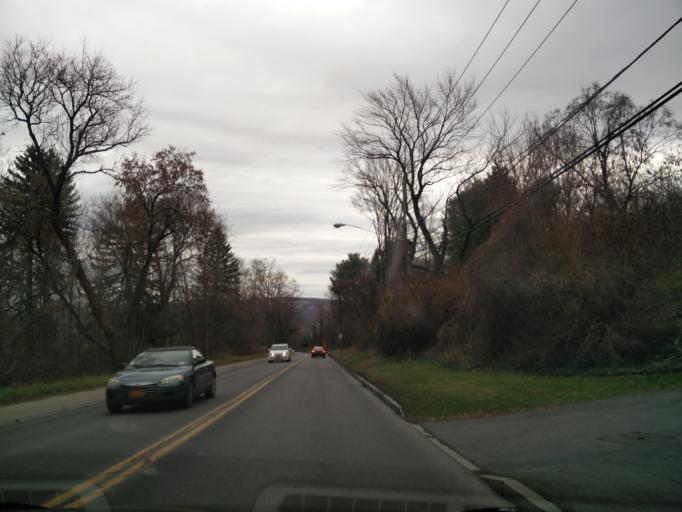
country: US
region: New York
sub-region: Tompkins County
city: Ithaca
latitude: 42.4523
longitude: -76.5195
